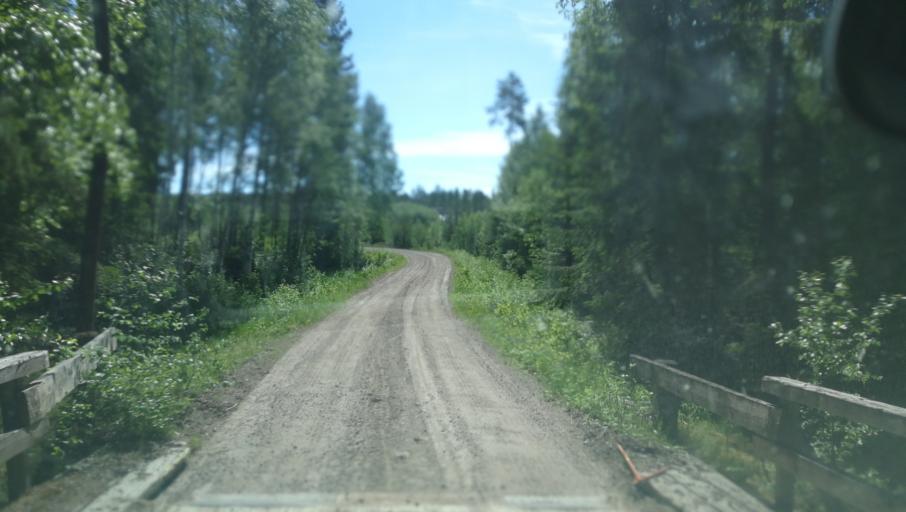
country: SE
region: Dalarna
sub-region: Vansbro Kommun
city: Vansbro
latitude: 60.8343
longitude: 14.1556
